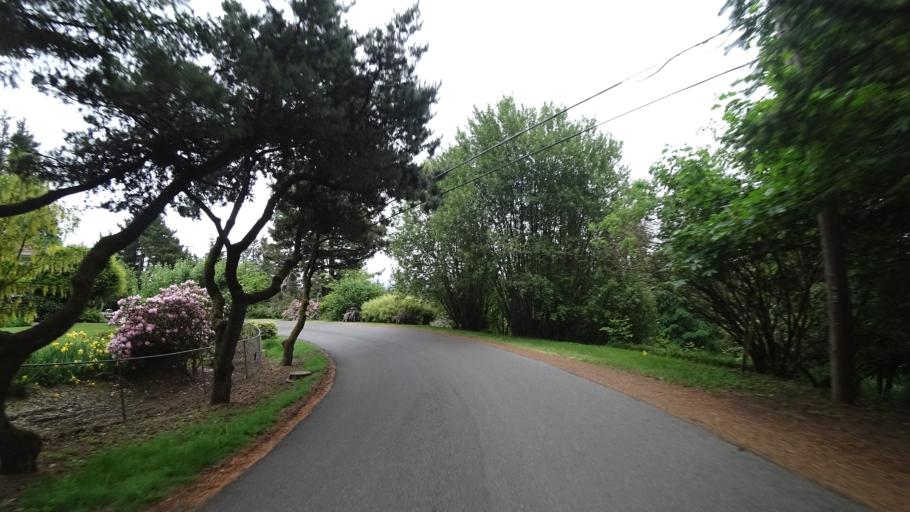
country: US
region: Oregon
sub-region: Multnomah County
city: Portland
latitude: 45.4870
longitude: -122.6947
